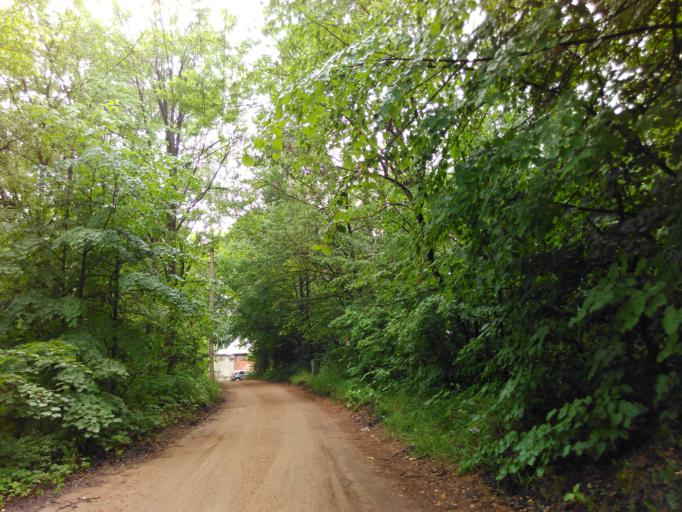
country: RU
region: Tverskaya
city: Ostashkov
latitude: 57.1686
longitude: 33.0935
